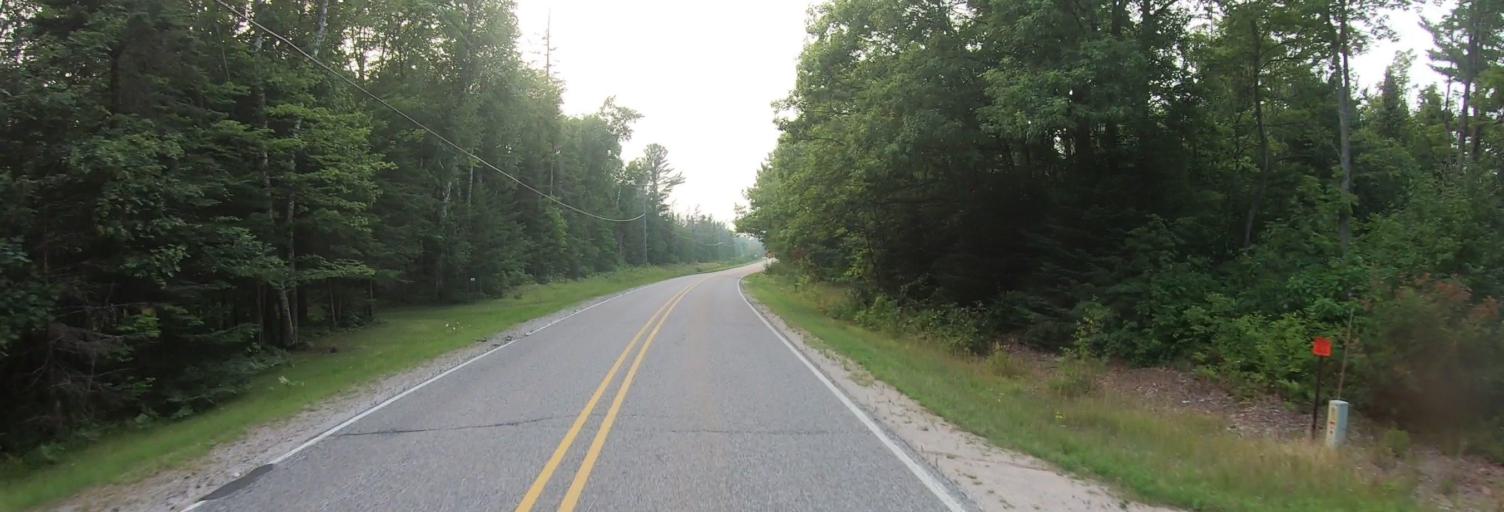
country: US
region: Michigan
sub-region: Chippewa County
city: Sault Ste. Marie
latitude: 46.4829
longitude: -84.6648
